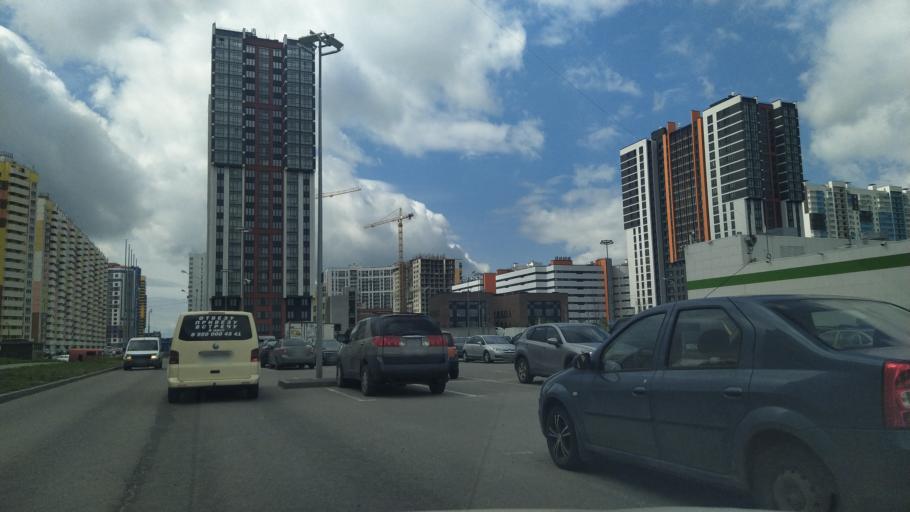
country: RU
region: Leningrad
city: Untolovo
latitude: 60.0374
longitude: 30.2374
